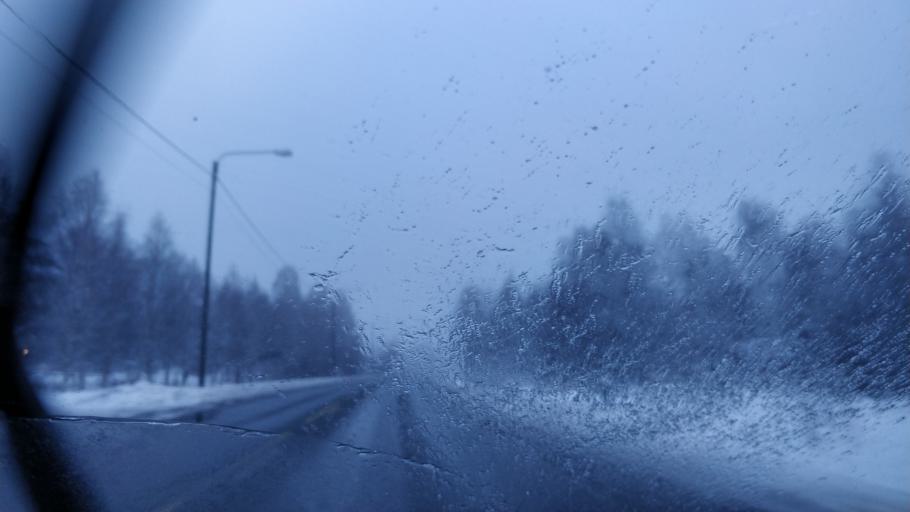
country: FI
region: Lapland
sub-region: Kemi-Tornio
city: Tervola
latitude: 66.1527
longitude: 24.9971
